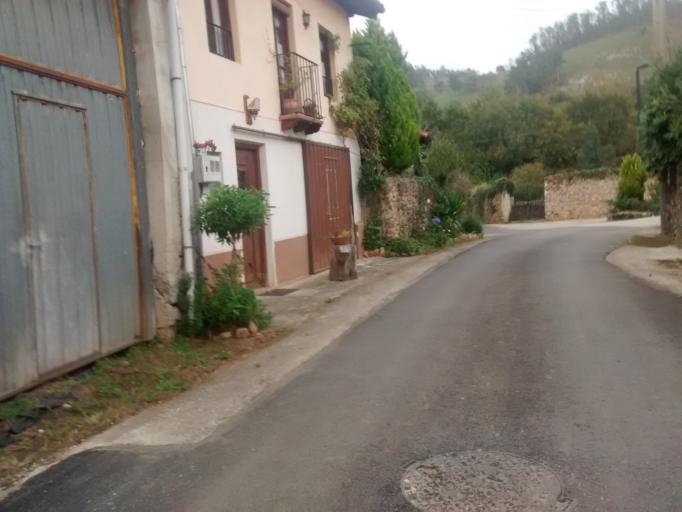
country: ES
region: Cantabria
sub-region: Provincia de Cantabria
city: Entrambasaguas
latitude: 43.3423
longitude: -3.6808
